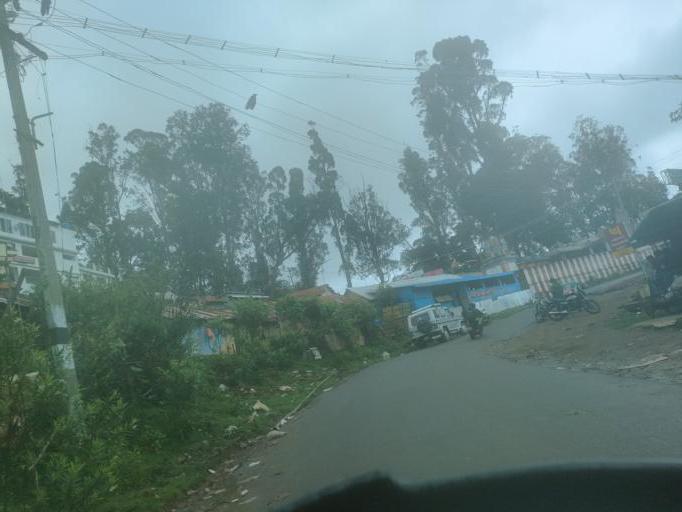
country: IN
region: Tamil Nadu
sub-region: Dindigul
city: Kodaikanal
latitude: 10.2277
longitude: 77.3513
